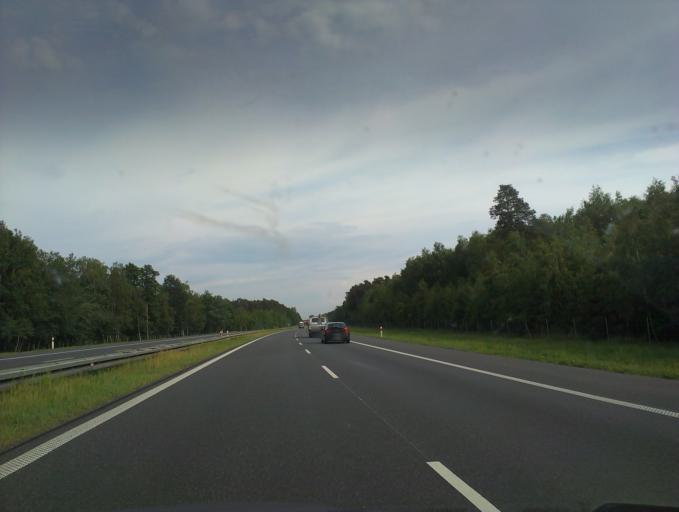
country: PL
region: Opole Voivodeship
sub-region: Powiat brzeski
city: Lewin Brzeski
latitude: 50.7035
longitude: 17.6158
